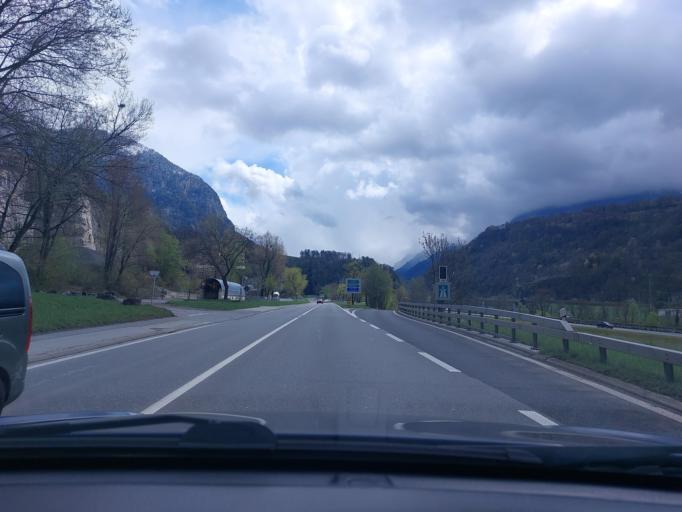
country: CH
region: Vaud
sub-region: Aigle District
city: Bex
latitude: 46.2370
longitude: 7.0014
